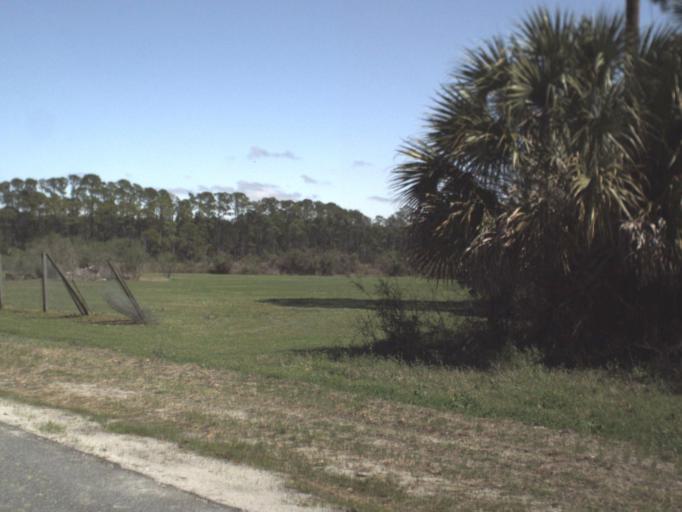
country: US
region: Florida
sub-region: Wakulla County
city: Crawfordville
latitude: 30.0377
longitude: -84.3879
